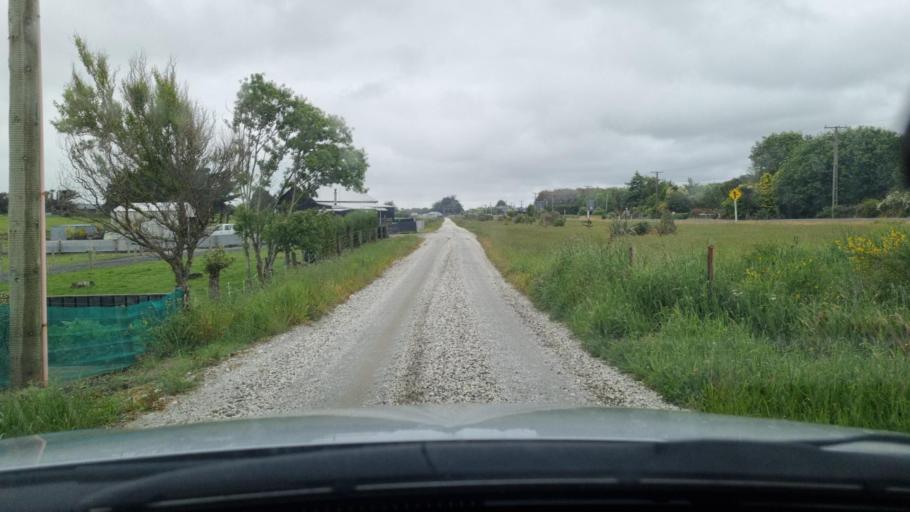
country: NZ
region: Southland
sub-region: Invercargill City
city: Invercargill
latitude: -46.4419
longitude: 168.3917
